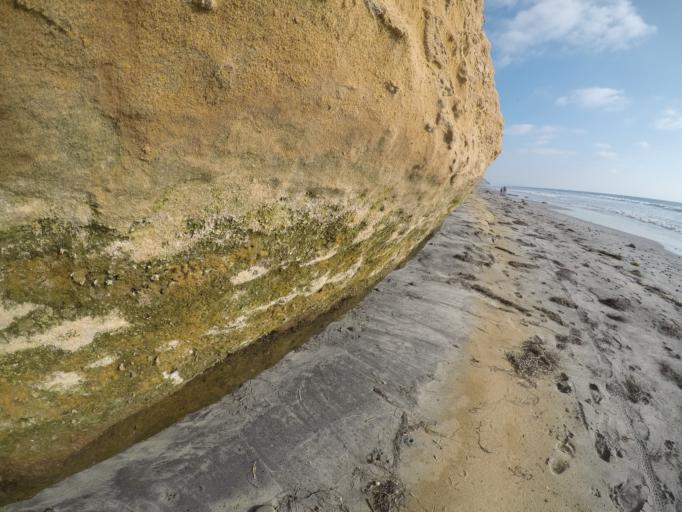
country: US
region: California
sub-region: San Diego County
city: Encinitas
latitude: 33.0539
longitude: -117.3007
